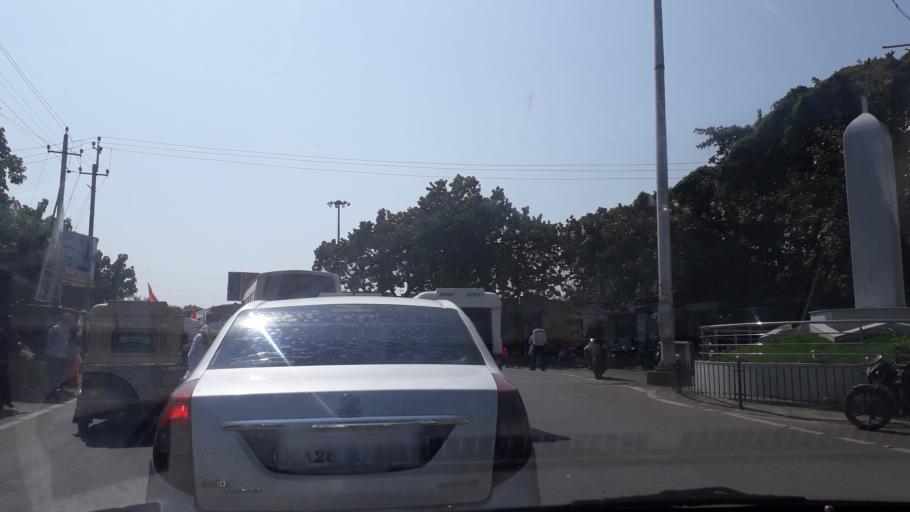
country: IN
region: Karnataka
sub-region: Bijapur
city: Bijapur
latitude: 16.8264
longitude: 75.7163
